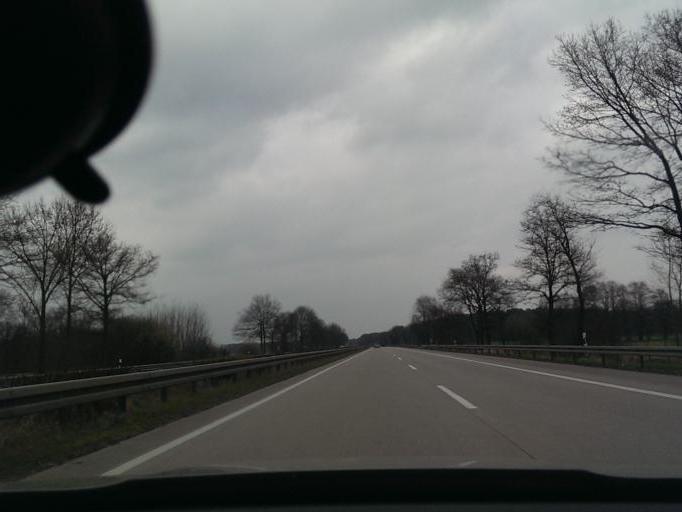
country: DE
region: Lower Saxony
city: Langenhagen
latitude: 52.4981
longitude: 9.7445
